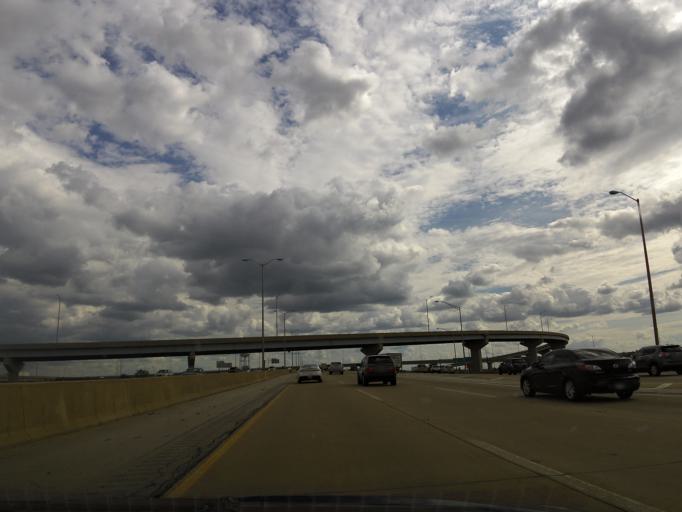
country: US
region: Illinois
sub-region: Will County
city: Bolingbrook
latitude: 41.7086
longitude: -88.0316
